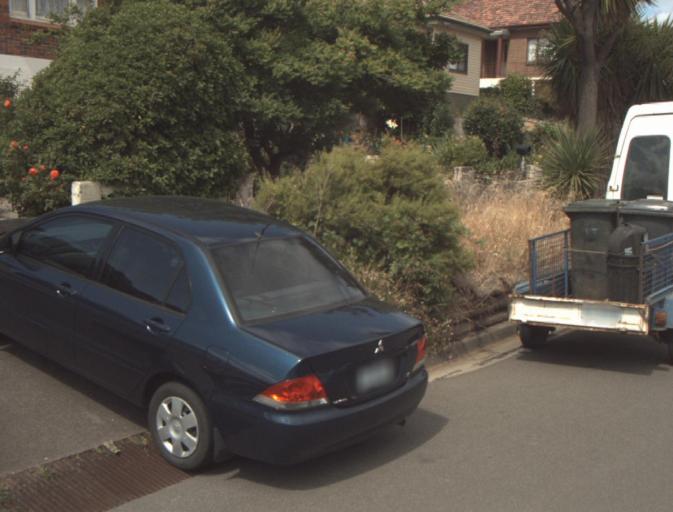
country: AU
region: Tasmania
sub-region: Launceston
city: Newstead
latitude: -41.4542
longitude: 147.1977
